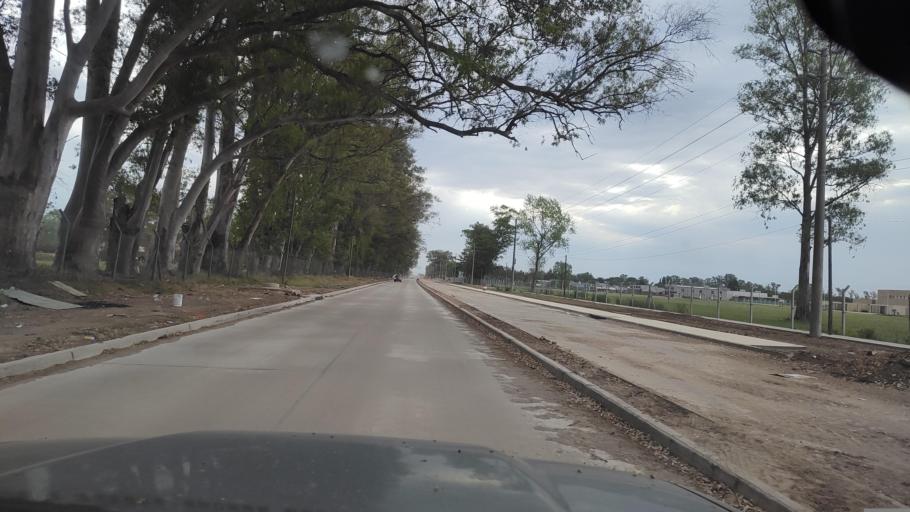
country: AR
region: Buenos Aires
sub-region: Partido de Lujan
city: Lujan
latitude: -34.5507
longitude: -59.0881
